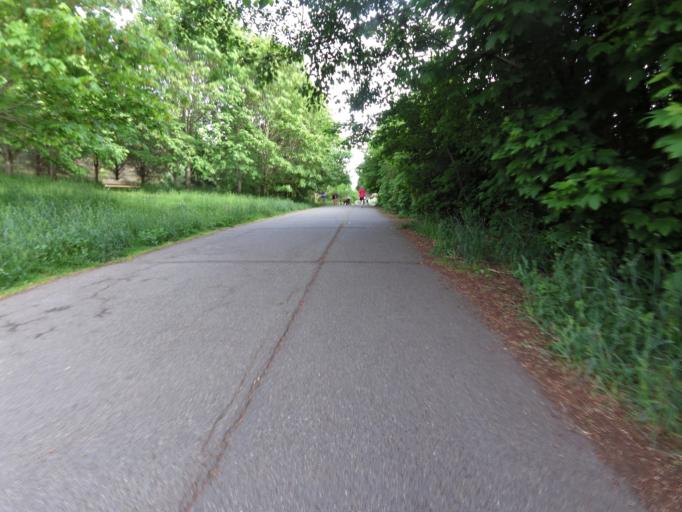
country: US
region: Washington
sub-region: King County
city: Seattle
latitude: 47.6550
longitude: -122.4136
